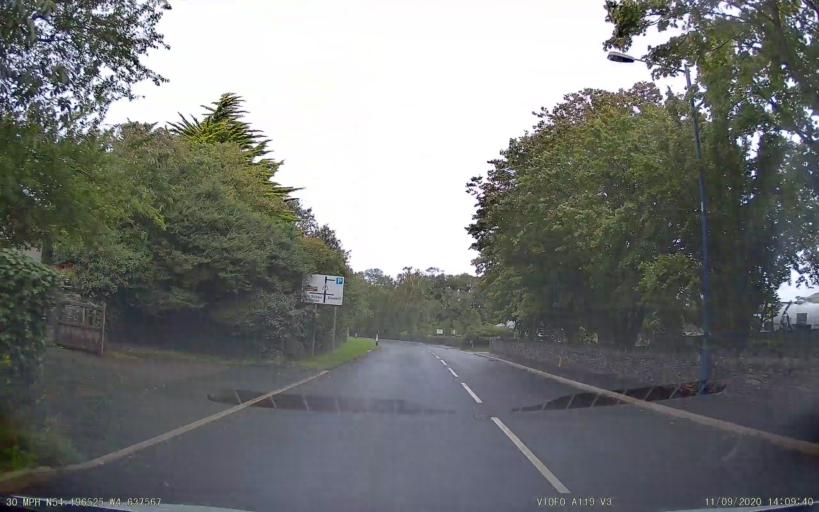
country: IM
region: Castletown
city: Castletown
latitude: 54.1965
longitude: -4.6376
